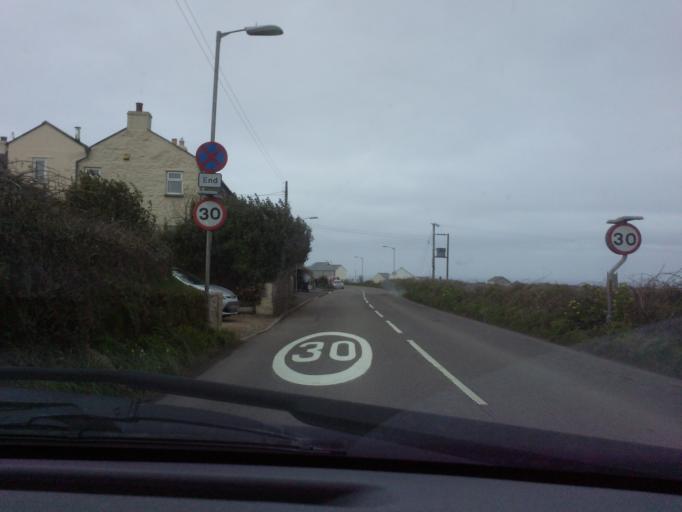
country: GB
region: England
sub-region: Cornwall
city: Saint Just
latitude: 50.1211
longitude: -5.6752
